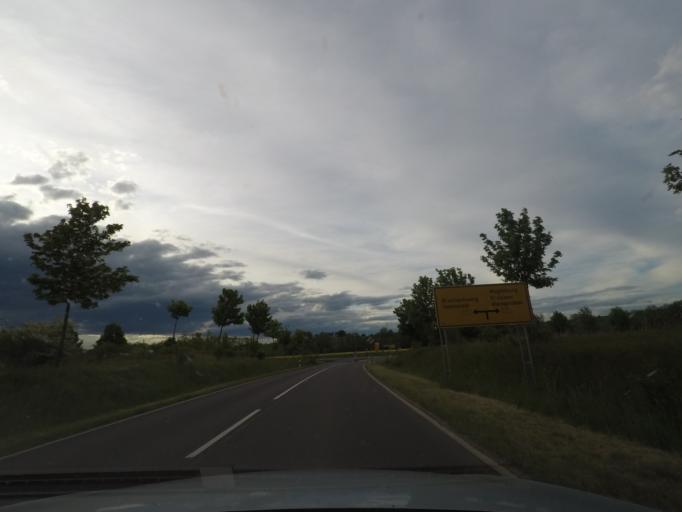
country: DE
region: Saxony-Anhalt
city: Wefensleben
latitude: 52.2110
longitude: 11.1315
